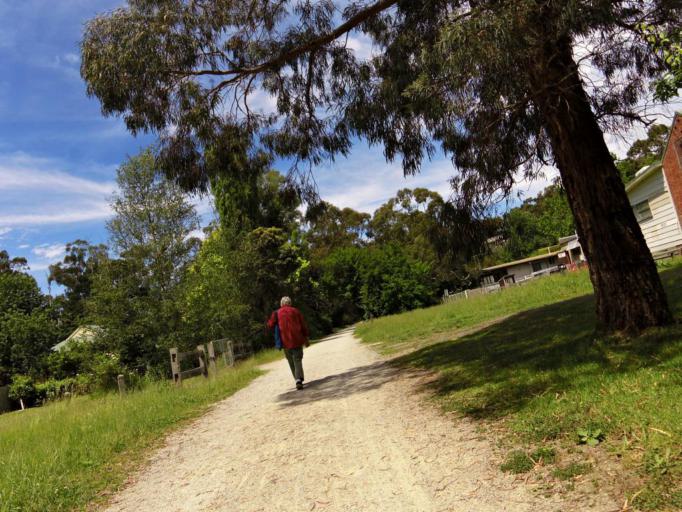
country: AU
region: Victoria
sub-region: Yarra Ranges
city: Yarra Junction
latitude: -37.7810
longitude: 145.6142
